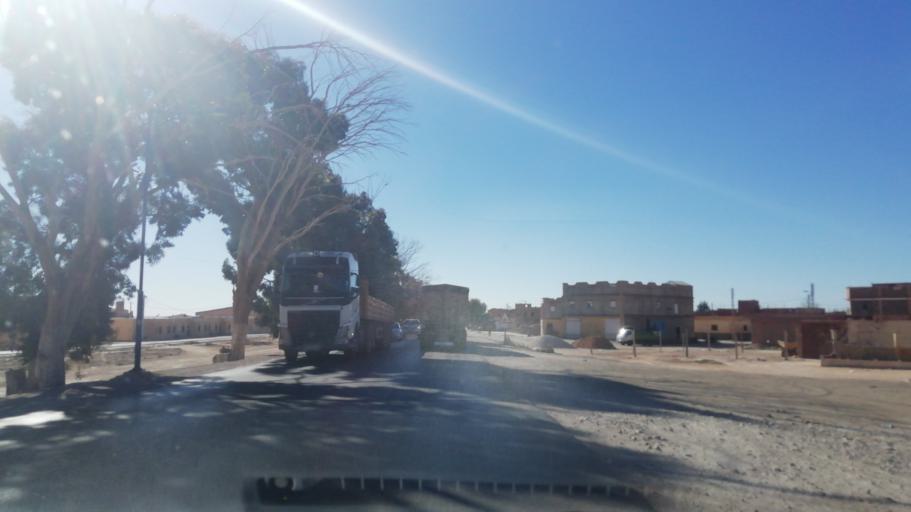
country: DZ
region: Saida
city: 'Ain el Hadjar
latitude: 34.1543
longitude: 0.0701
